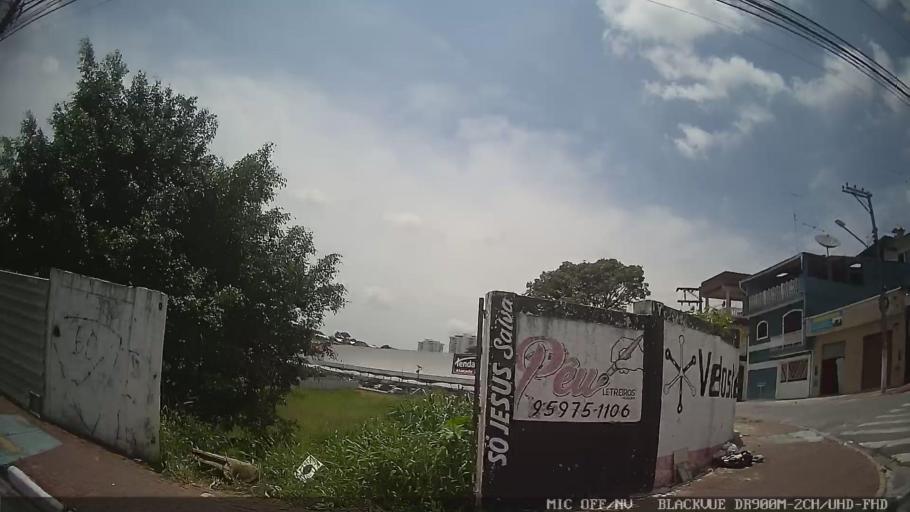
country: BR
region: Sao Paulo
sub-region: Ferraz De Vasconcelos
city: Ferraz de Vasconcelos
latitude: -23.5491
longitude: -46.3783
